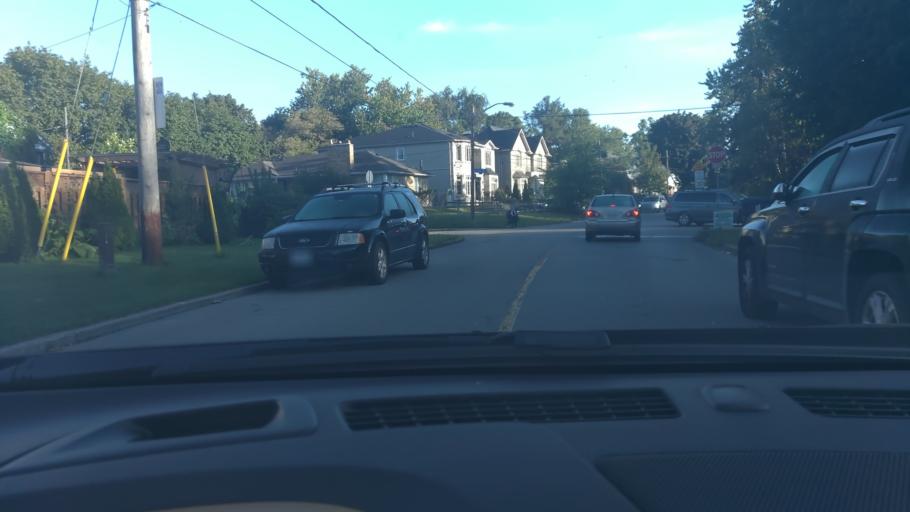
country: CA
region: Ontario
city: Toronto
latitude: 43.7220
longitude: -79.4342
